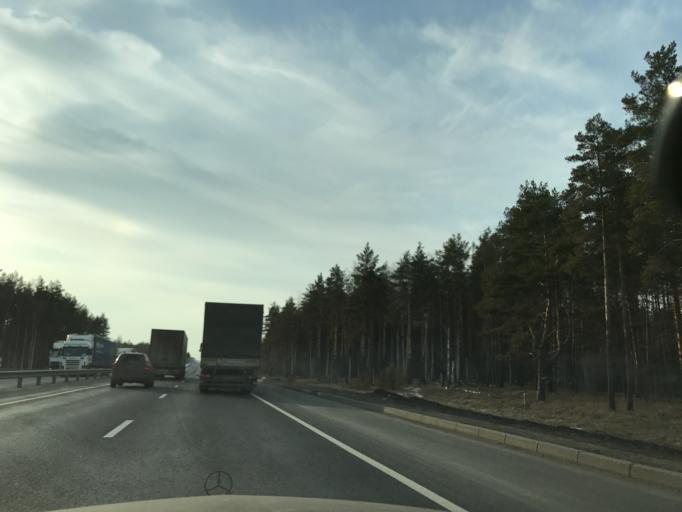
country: RU
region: Vladimir
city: Orgtrud
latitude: 56.1026
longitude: 40.7467
